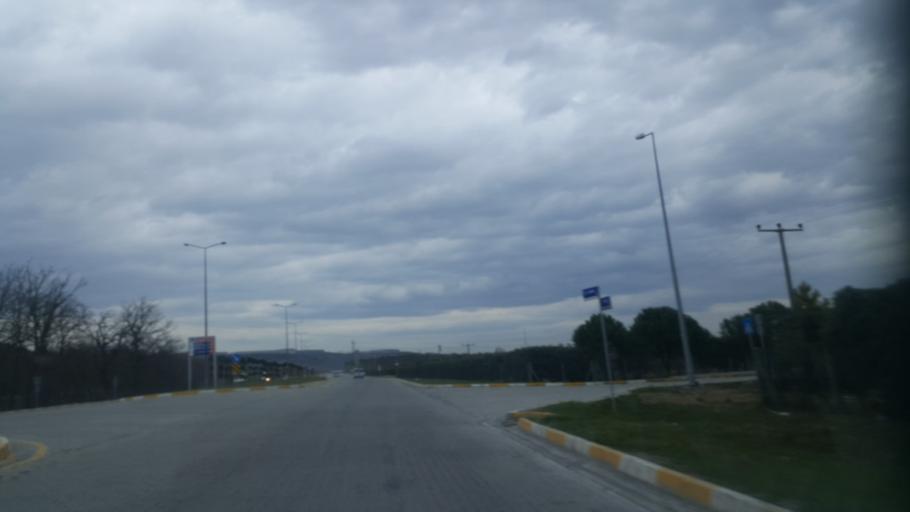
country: TR
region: Kocaeli
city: Mollafeneri
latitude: 40.8680
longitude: 29.5593
